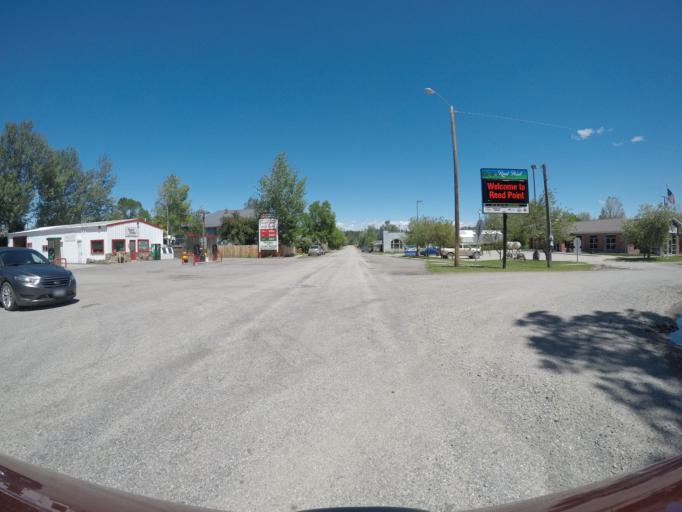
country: US
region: Montana
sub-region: Stillwater County
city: Absarokee
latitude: 45.7066
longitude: -109.5419
